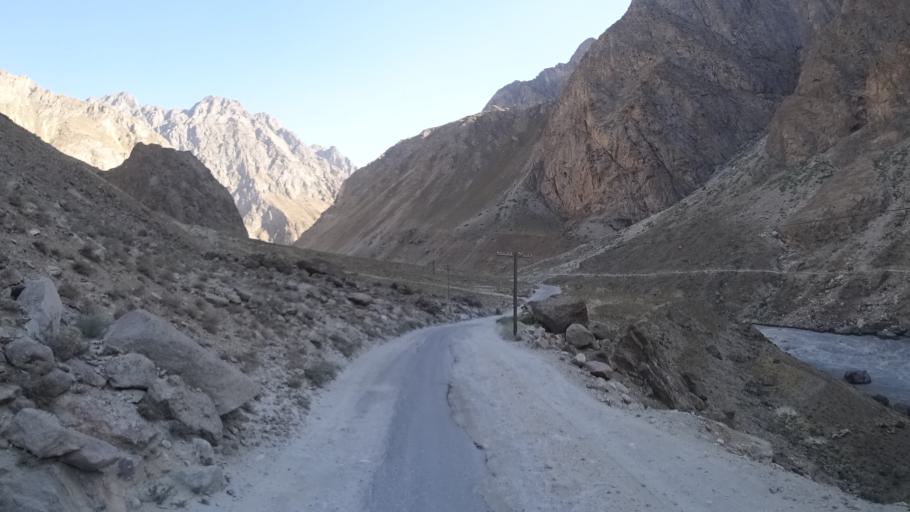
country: TJ
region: Gorno-Badakhshan
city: Rushon
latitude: 37.9854
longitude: 71.2693
